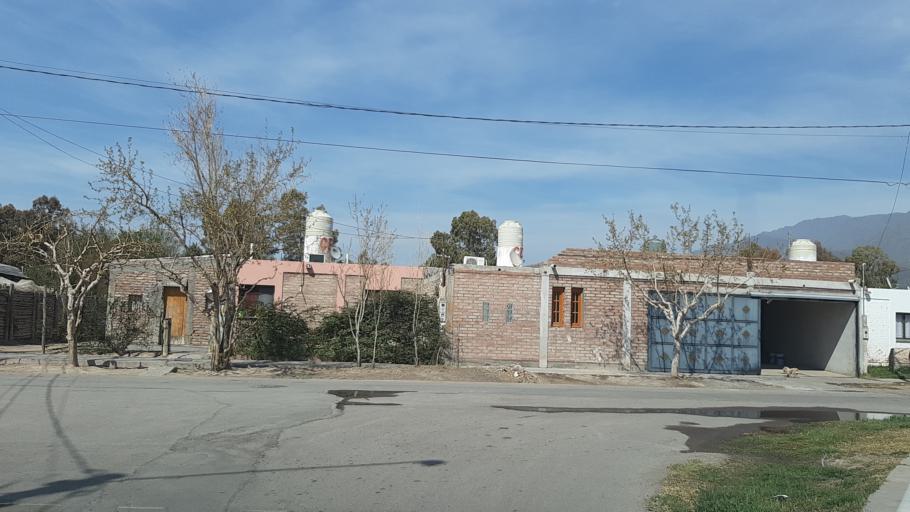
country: AR
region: San Juan
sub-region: Departamento de Zonda
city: Zonda
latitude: -31.5410
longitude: -68.7504
